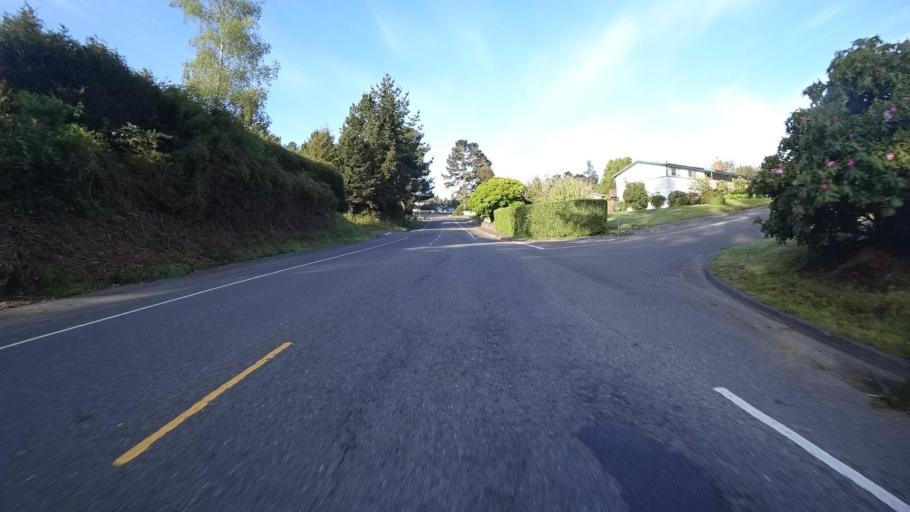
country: US
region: California
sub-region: Humboldt County
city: Humboldt Hill
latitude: 40.7222
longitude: -124.2016
